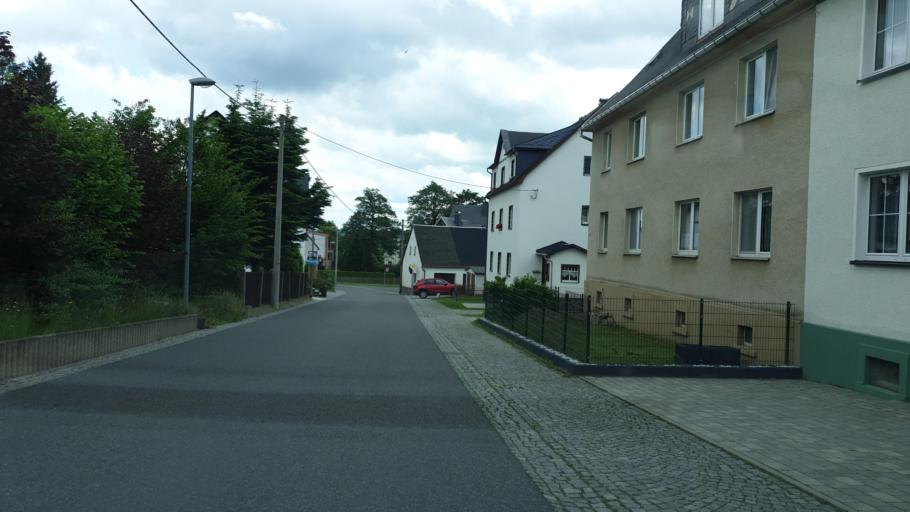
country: DE
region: Saxony
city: Marienberg
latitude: 50.6788
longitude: 13.1745
